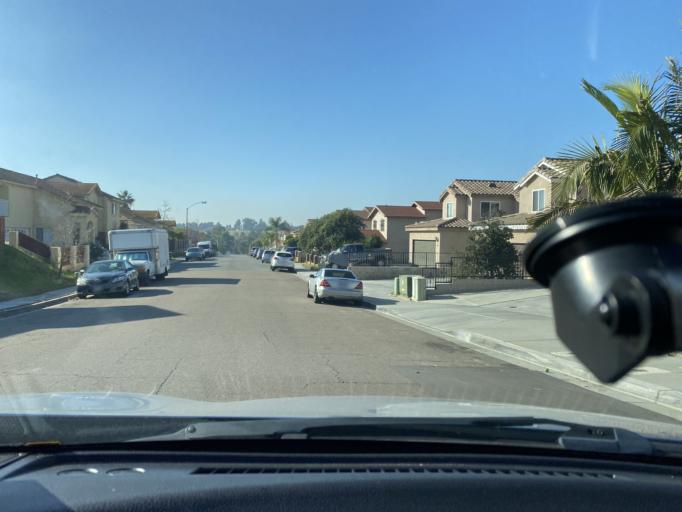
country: US
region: California
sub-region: San Diego County
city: National City
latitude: 32.7060
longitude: -117.0895
